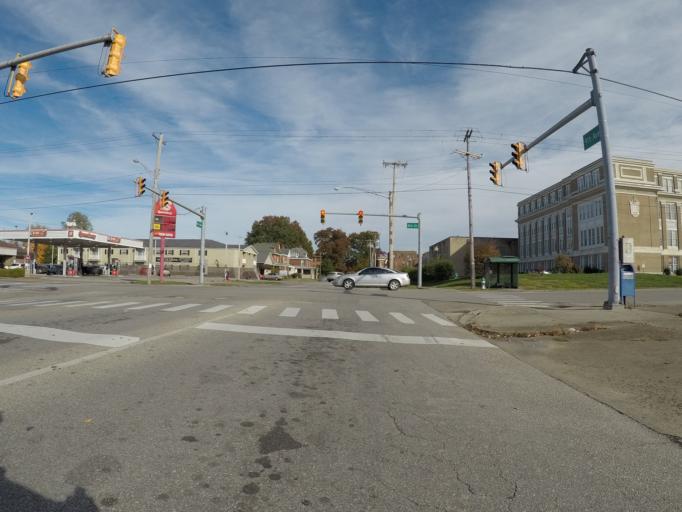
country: US
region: West Virginia
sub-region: Cabell County
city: Huntington
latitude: 38.4134
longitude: -82.4438
